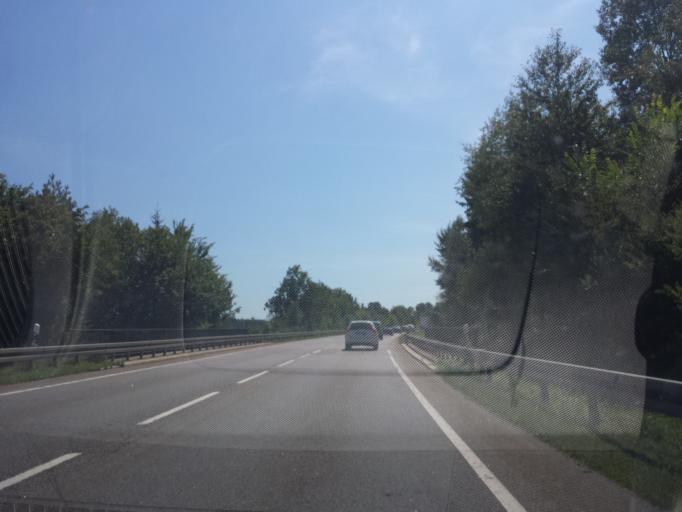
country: DE
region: Bavaria
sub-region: Lower Bavaria
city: Rattiszell
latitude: 49.0341
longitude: 12.6543
